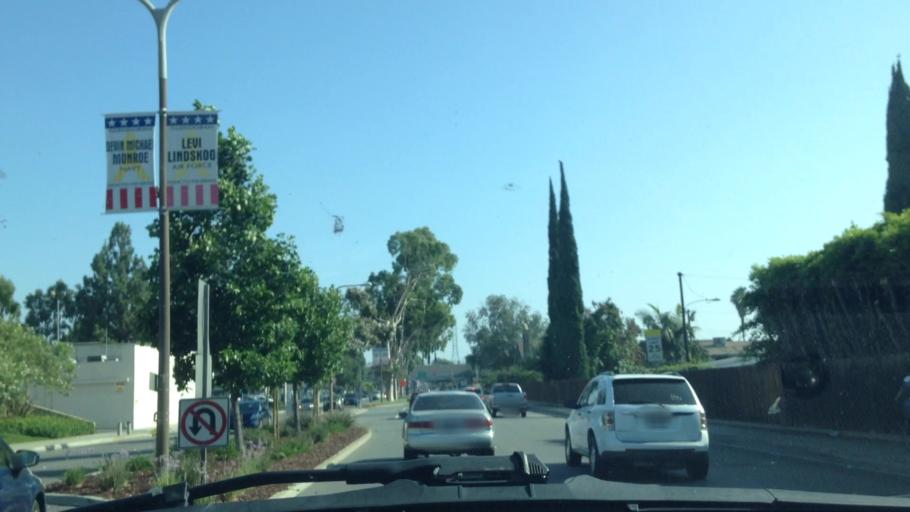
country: US
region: California
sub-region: Los Angeles County
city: Glendora
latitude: 34.1243
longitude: -117.8727
